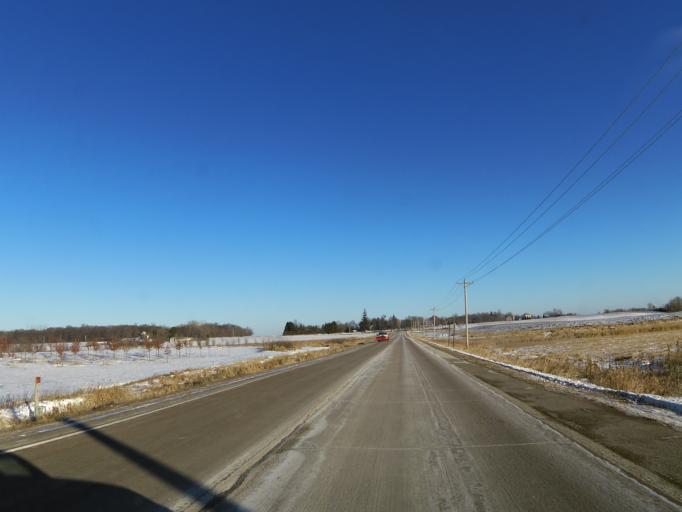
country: US
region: Minnesota
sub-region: Scott County
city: Jordan
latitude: 44.6545
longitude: -93.5623
